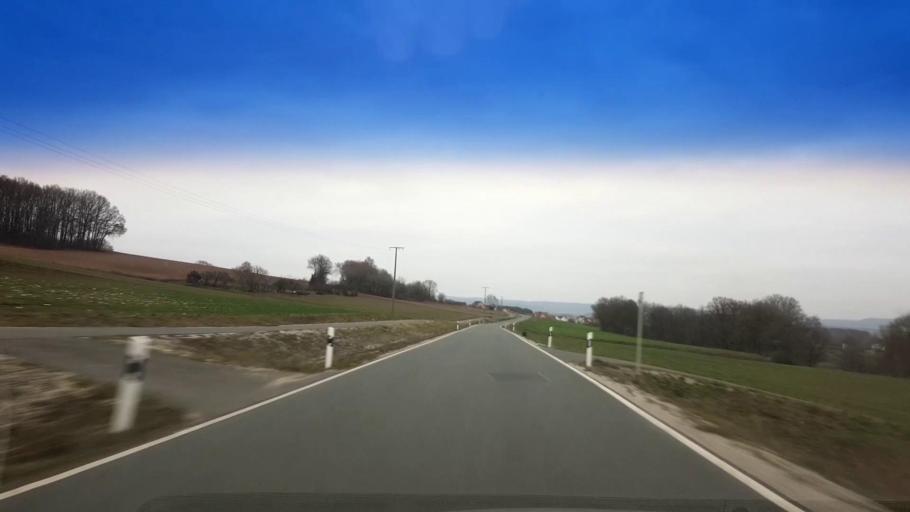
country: DE
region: Bavaria
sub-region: Upper Franconia
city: Hallerndorf
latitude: 49.7673
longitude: 10.9923
